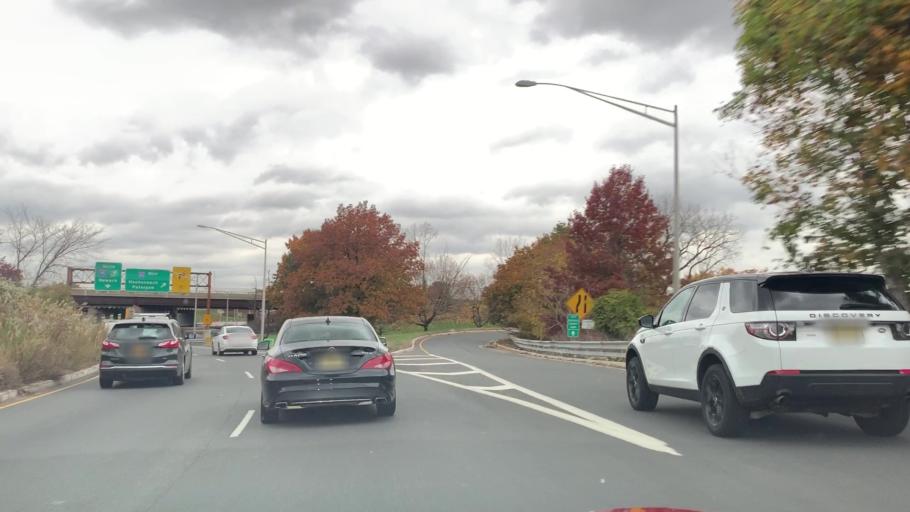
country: US
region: New Jersey
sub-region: Bergen County
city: Ridgefield Park
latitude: 40.8468
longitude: -74.0150
